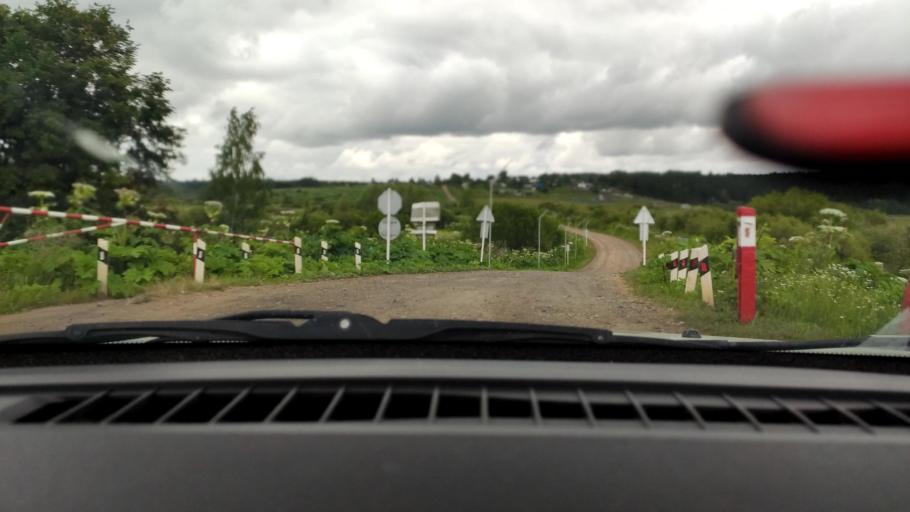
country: RU
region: Perm
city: Chaykovskaya
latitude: 58.1341
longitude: 55.5580
